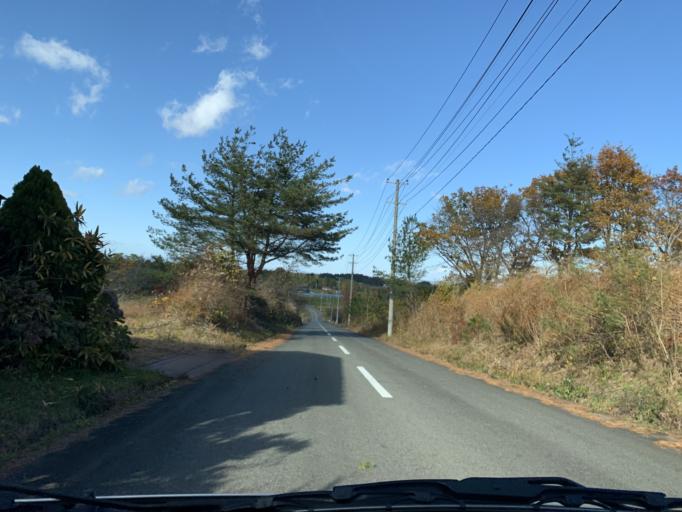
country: JP
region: Iwate
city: Mizusawa
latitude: 39.0629
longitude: 141.1127
